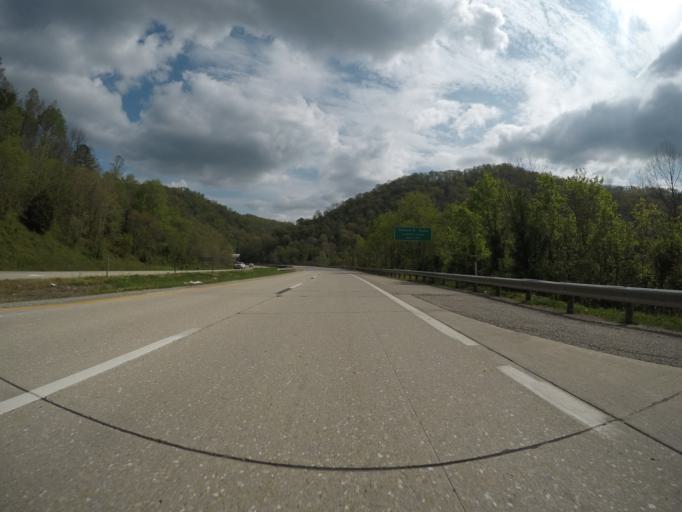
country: US
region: West Virginia
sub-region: Boone County
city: Madison
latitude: 38.1334
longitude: -81.8367
